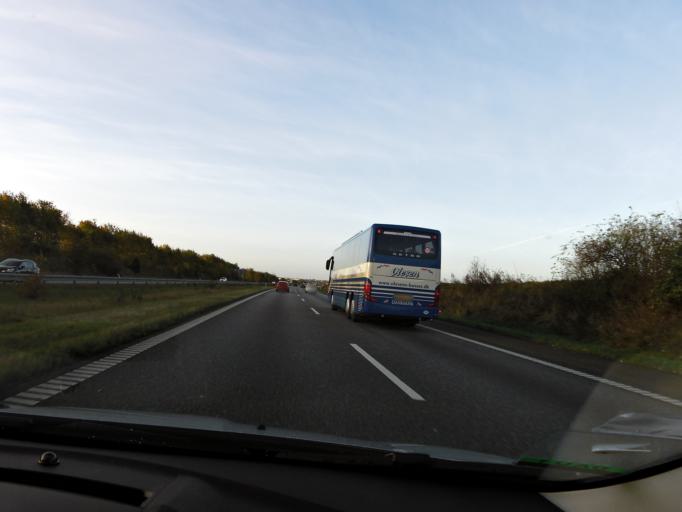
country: DK
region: Central Jutland
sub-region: Skanderborg Kommune
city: Stilling
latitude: 56.0790
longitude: 10.0068
